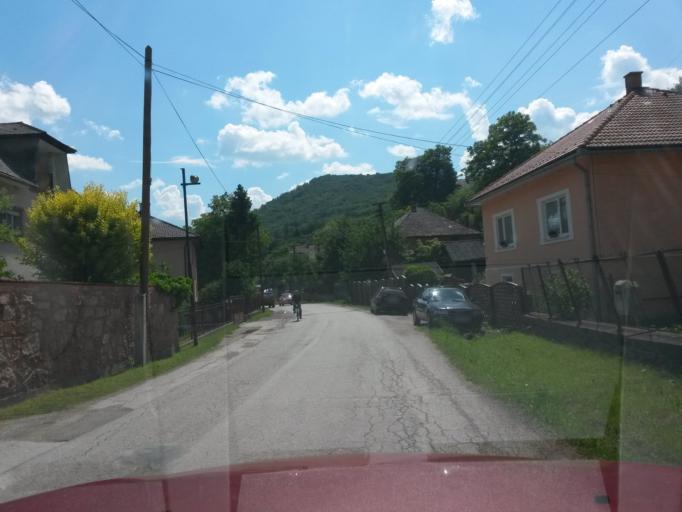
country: SK
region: Kosicky
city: Roznava
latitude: 48.6869
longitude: 20.5427
